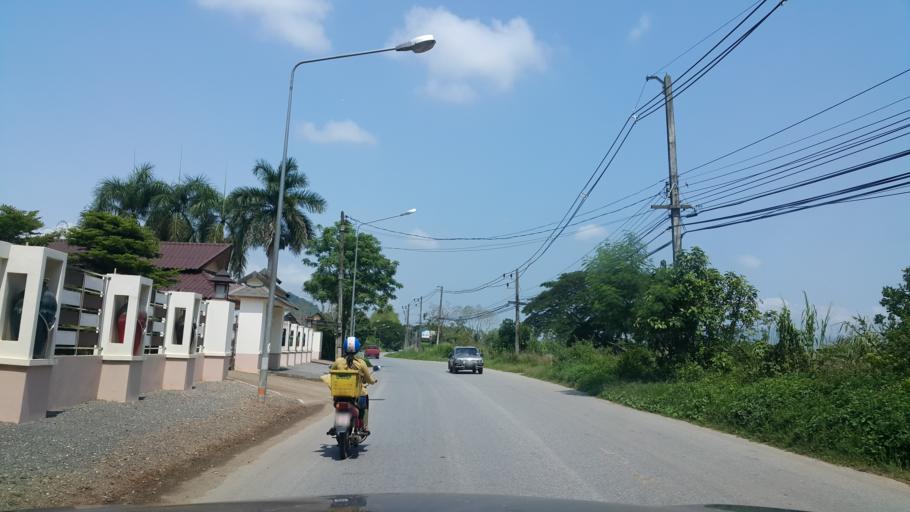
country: TH
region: Chiang Rai
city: Chiang Rai
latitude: 19.9315
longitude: 99.8239
